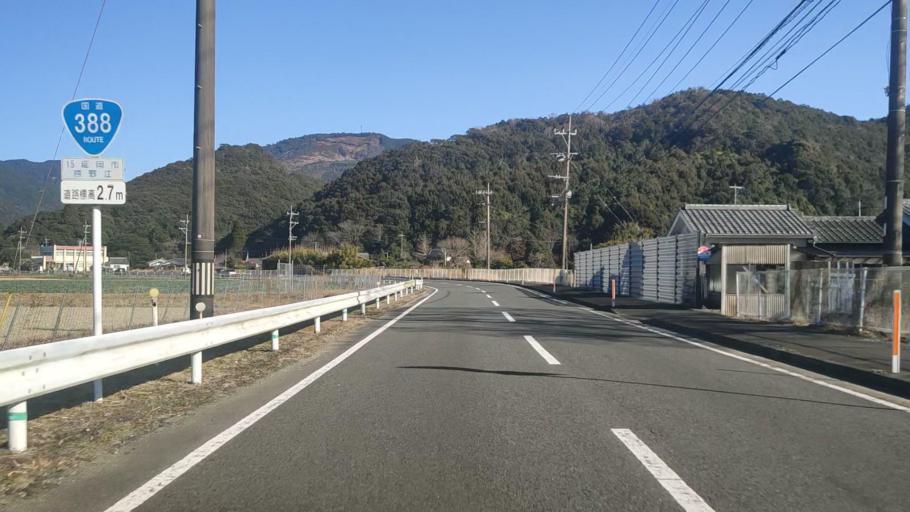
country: JP
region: Miyazaki
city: Nobeoka
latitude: 32.6809
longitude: 131.7870
